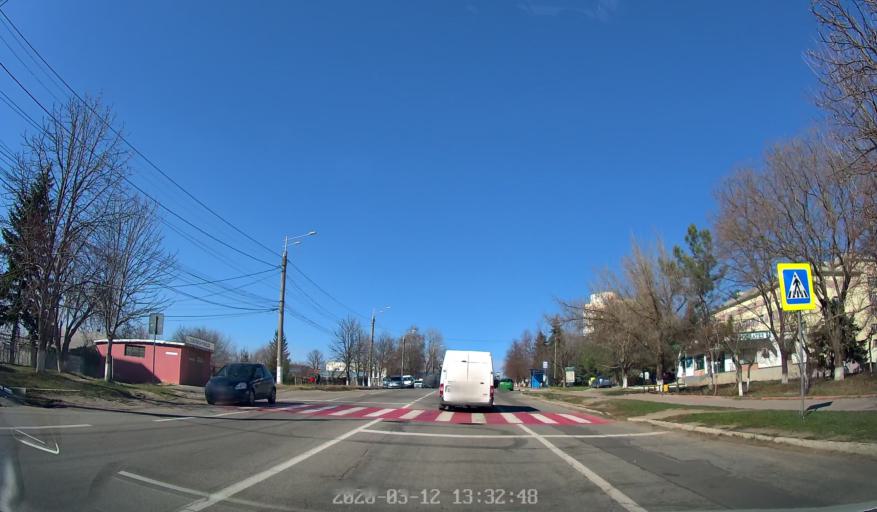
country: MD
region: Laloveni
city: Ialoveni
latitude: 46.9531
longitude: 28.7706
